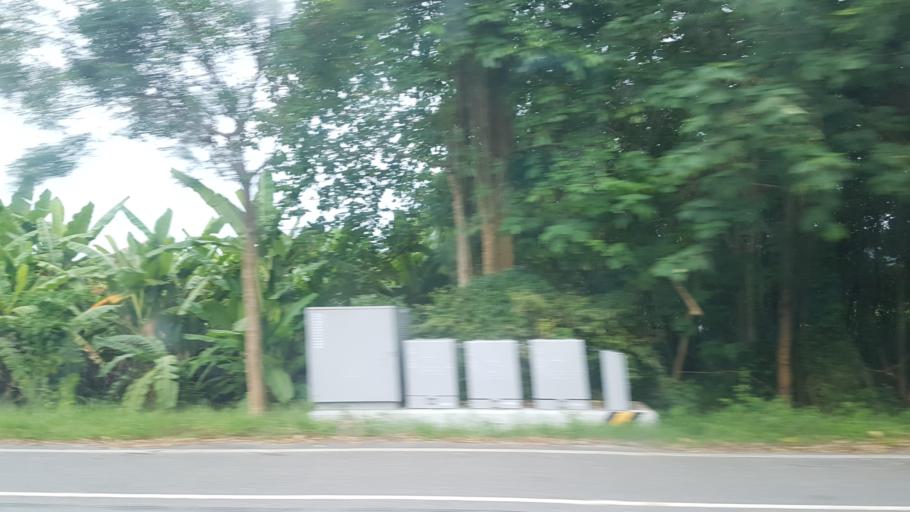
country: TW
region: Taiwan
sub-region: Hualien
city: Hualian
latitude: 23.8861
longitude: 121.5454
